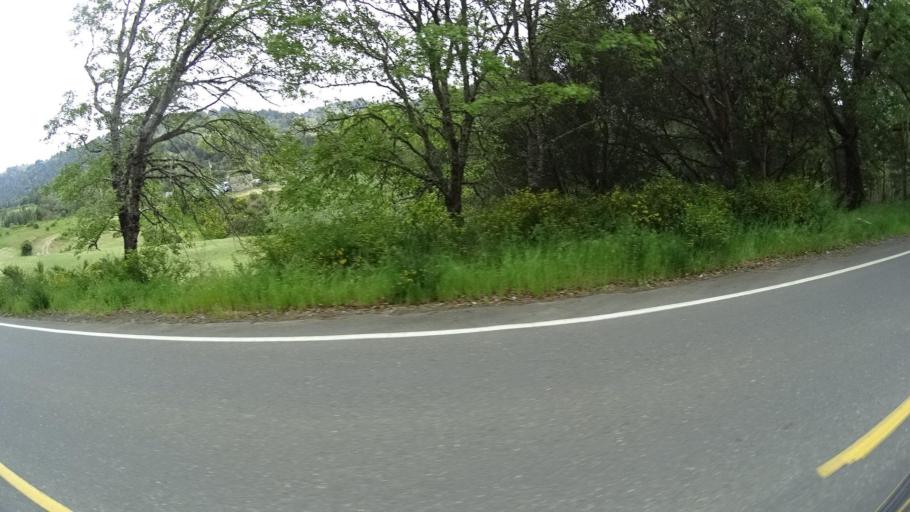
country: US
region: California
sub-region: Humboldt County
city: Redway
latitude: 40.1066
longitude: -123.7855
